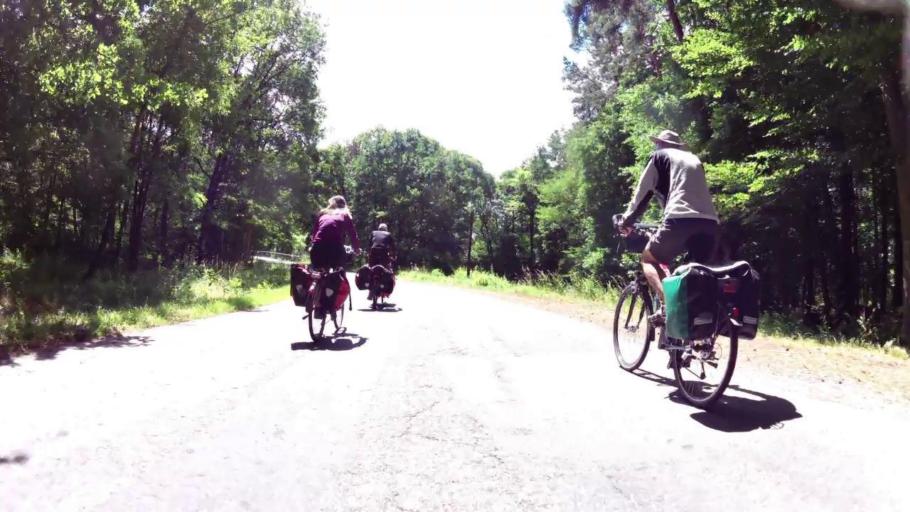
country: PL
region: West Pomeranian Voivodeship
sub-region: Powiat lobeski
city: Resko
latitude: 53.7515
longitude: 15.5035
